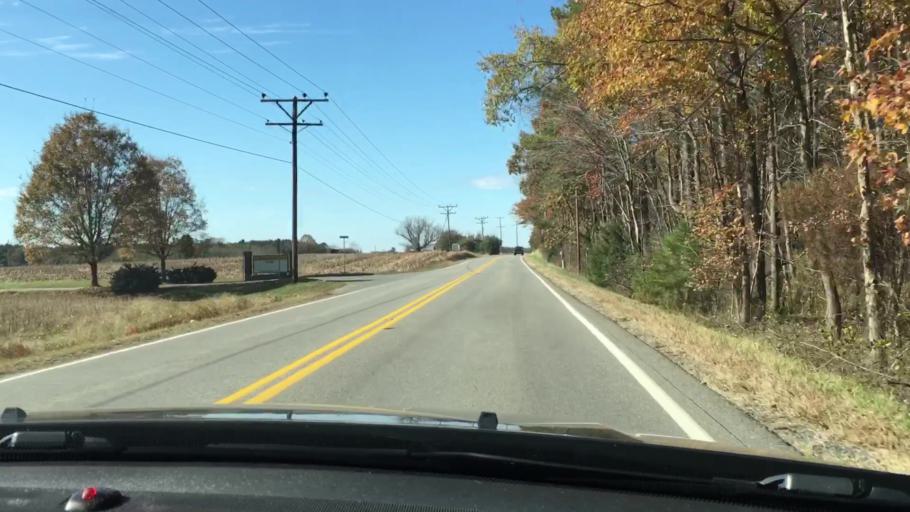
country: US
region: Virginia
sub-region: King William County
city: Central Garage
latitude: 37.7222
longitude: -77.0847
